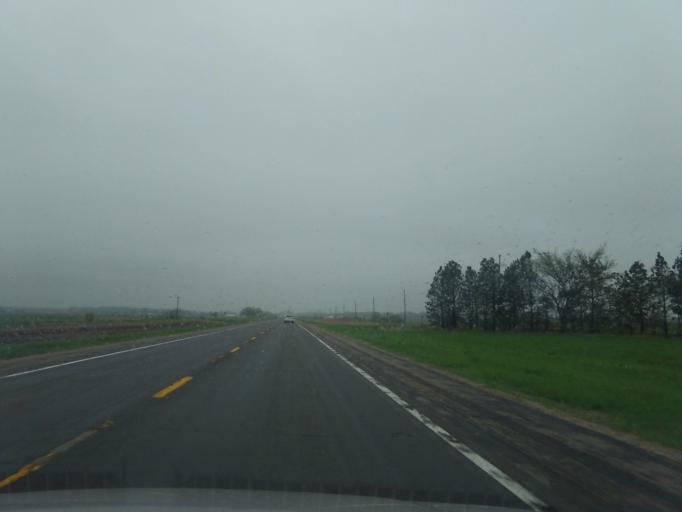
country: US
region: Nebraska
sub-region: Cuming County
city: West Point
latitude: 41.9158
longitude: -96.7896
